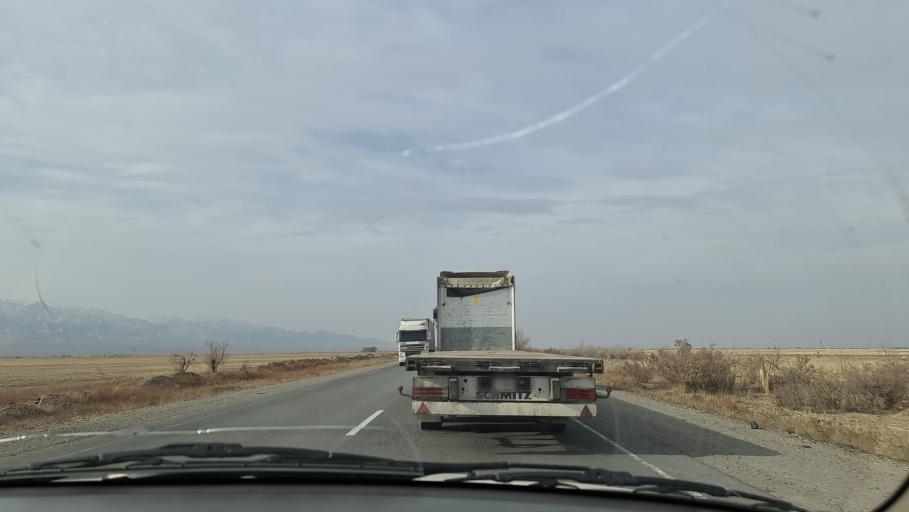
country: KG
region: Chuy
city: Tokmok
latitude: 43.3471
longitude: 75.5034
